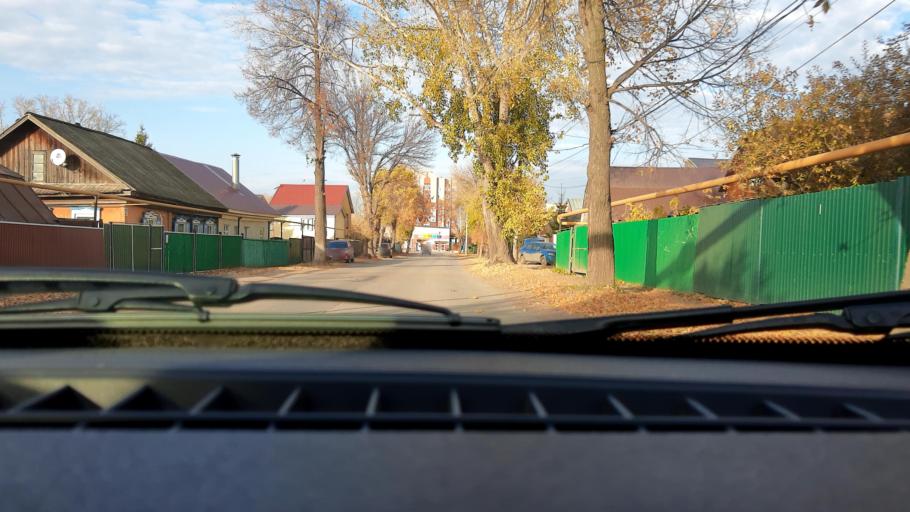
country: RU
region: Bashkortostan
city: Mikhaylovka
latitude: 54.7391
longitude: 55.8989
